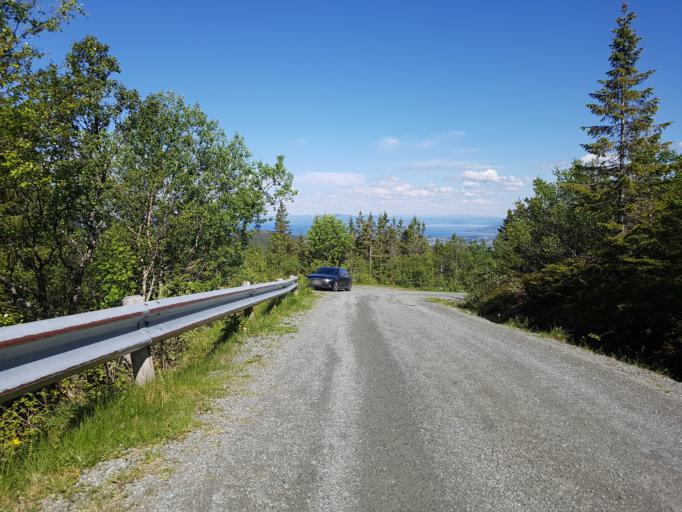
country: NO
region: Sor-Trondelag
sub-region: Trondheim
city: Trondheim
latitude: 63.4219
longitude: 10.2578
